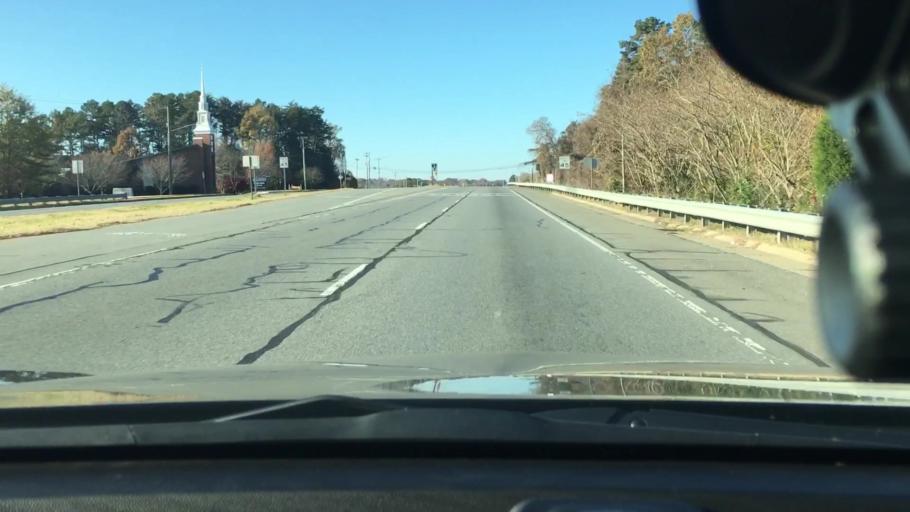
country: US
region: North Carolina
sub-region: Cabarrus County
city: Concord
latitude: 35.3666
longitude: -80.5800
